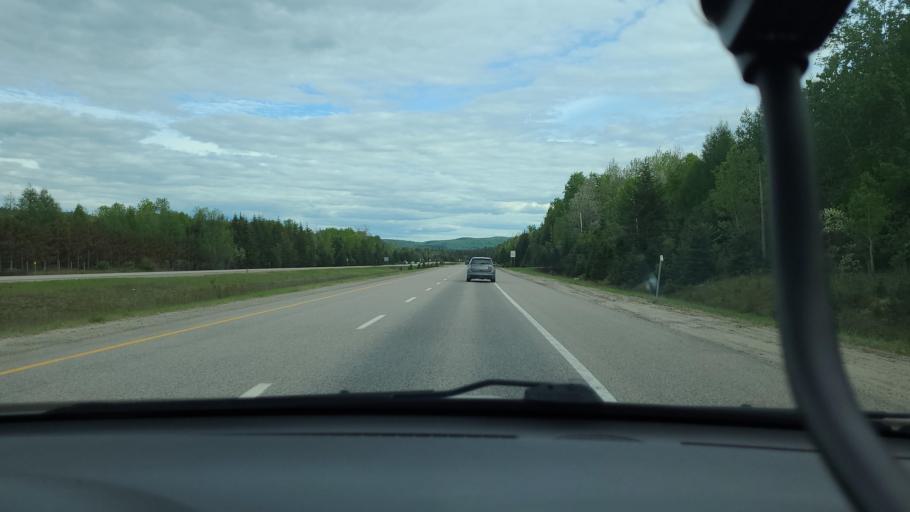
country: CA
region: Quebec
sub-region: Laurentides
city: Labelle
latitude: 46.2509
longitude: -74.7198
